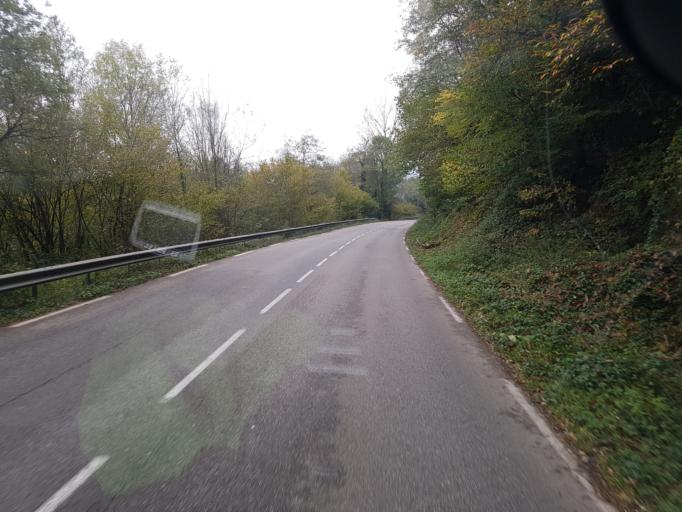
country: FR
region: Rhone-Alpes
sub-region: Departement de la Savoie
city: Saint-Genix-sur-Guiers
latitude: 45.6143
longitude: 5.6533
